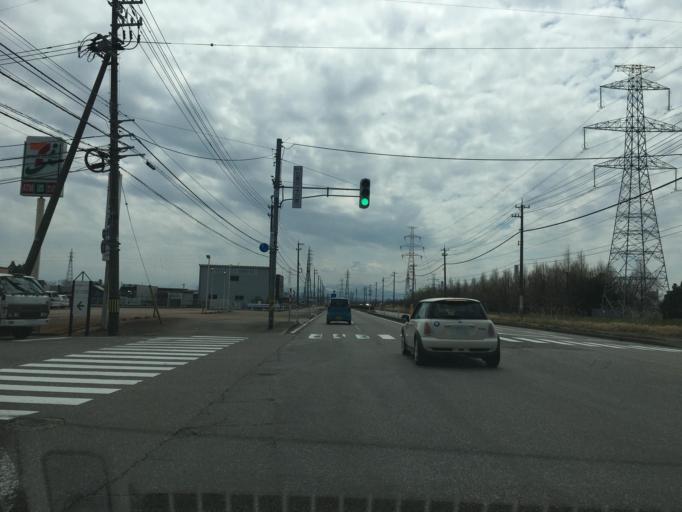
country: JP
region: Toyama
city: Kuragaki-kosugi
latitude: 36.7518
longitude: 137.1312
